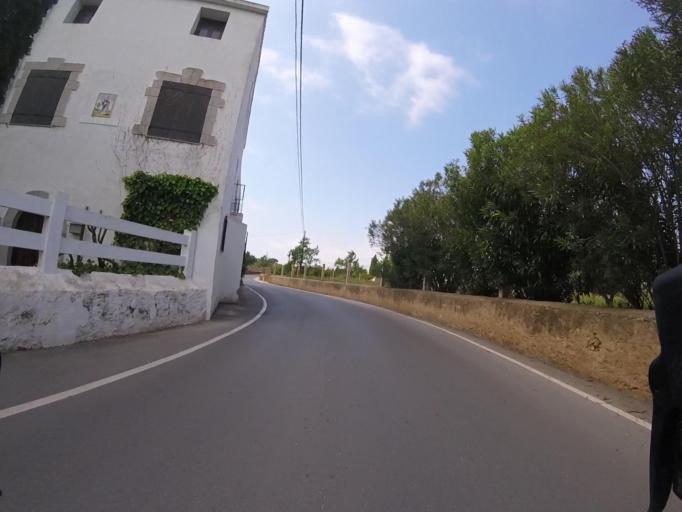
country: ES
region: Valencia
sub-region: Provincia de Castello
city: Alcoceber
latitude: 40.2422
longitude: 0.2712
